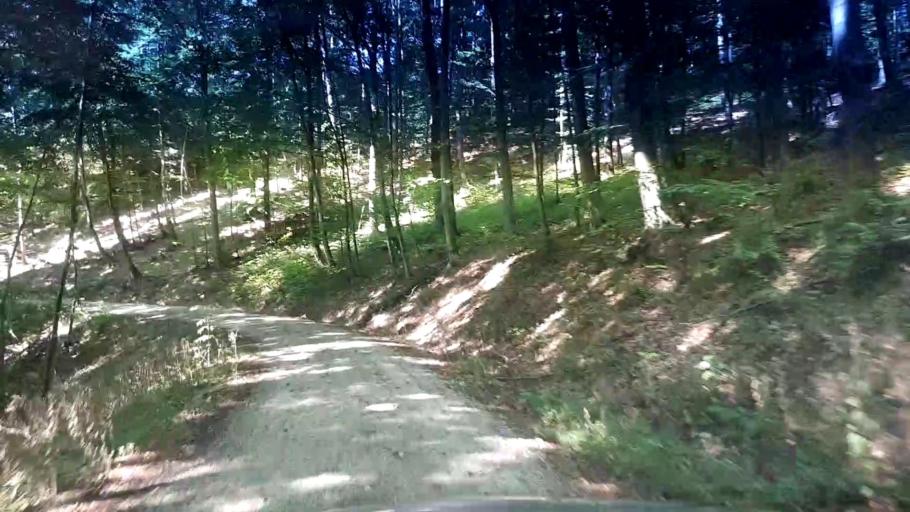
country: DE
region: Bavaria
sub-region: Upper Franconia
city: Litzendorf
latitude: 49.8824
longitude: 11.0368
